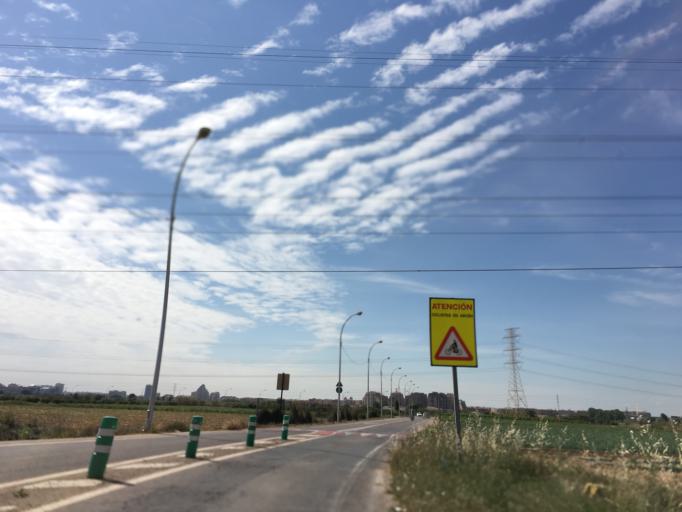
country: ES
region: Valencia
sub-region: Provincia de Valencia
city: Paterna
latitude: 39.4935
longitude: -0.4182
